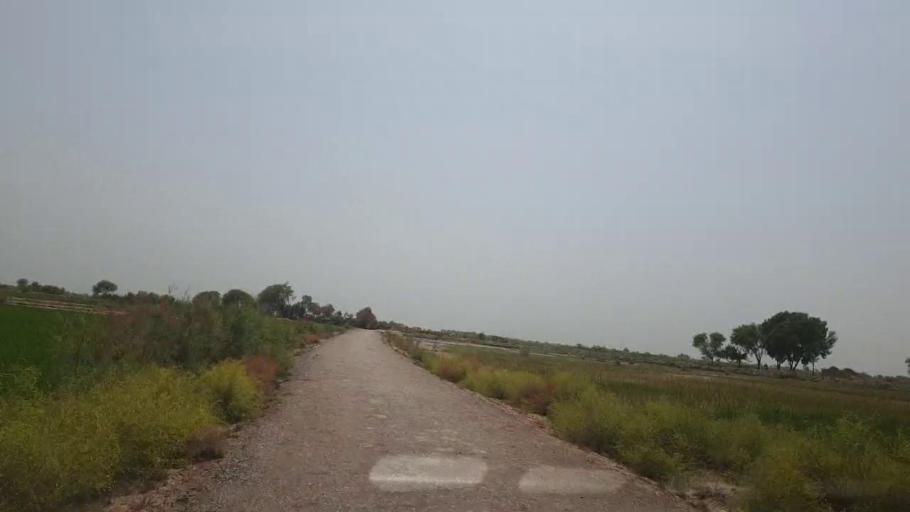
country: PK
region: Sindh
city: Garhi Yasin
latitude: 28.0578
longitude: 68.3167
